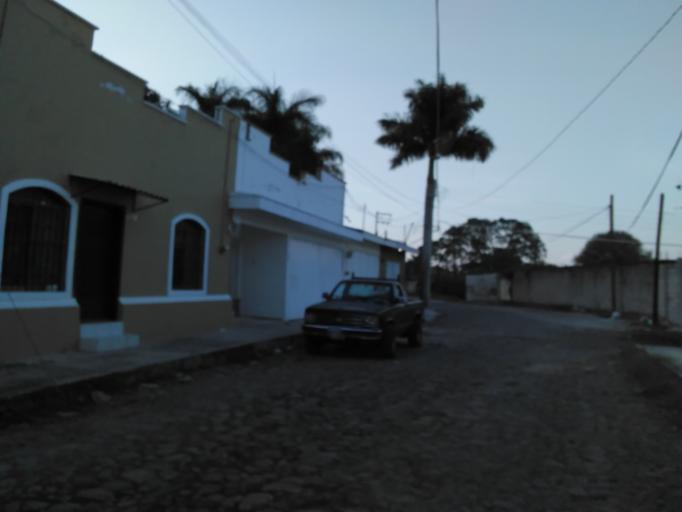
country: MX
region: Nayarit
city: Tepic
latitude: 21.5083
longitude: -104.9205
